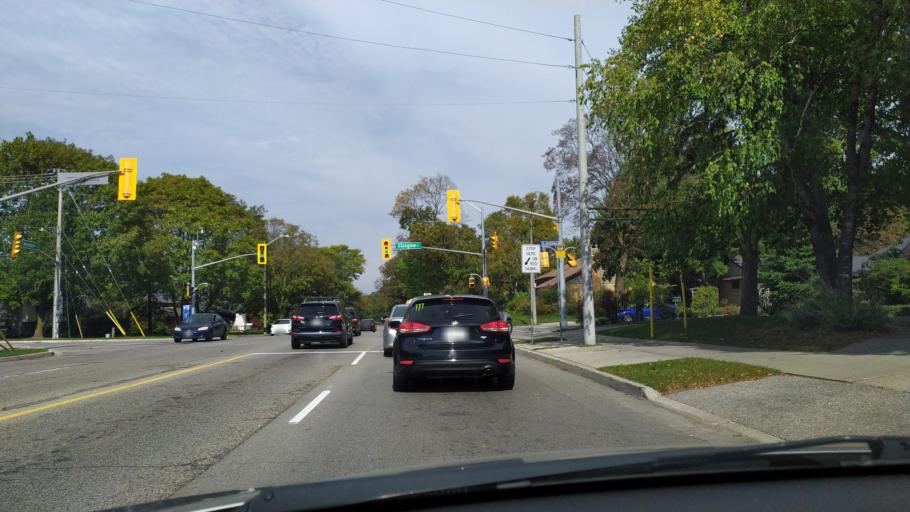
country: CA
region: Ontario
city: Waterloo
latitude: 43.4492
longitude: -80.5235
